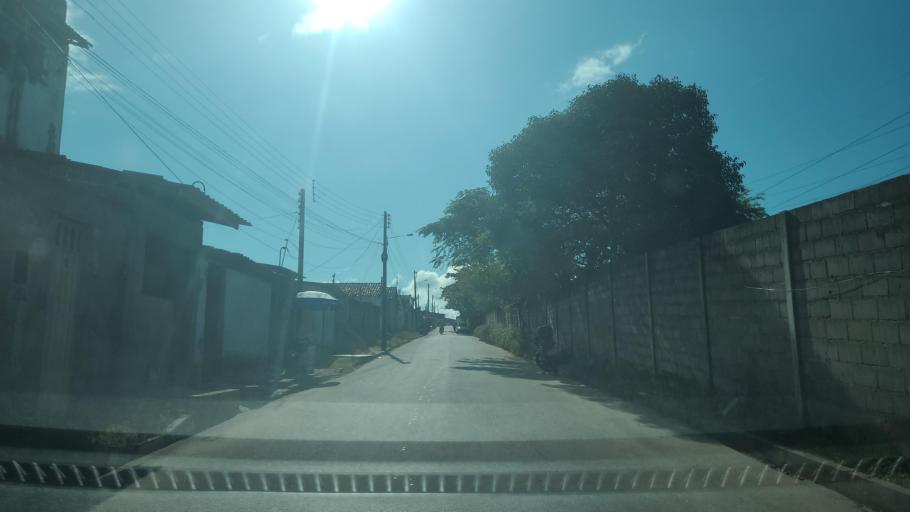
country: BR
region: Alagoas
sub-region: Uniao Dos Palmares
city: Uniao dos Palmares
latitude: -9.1568
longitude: -36.0203
